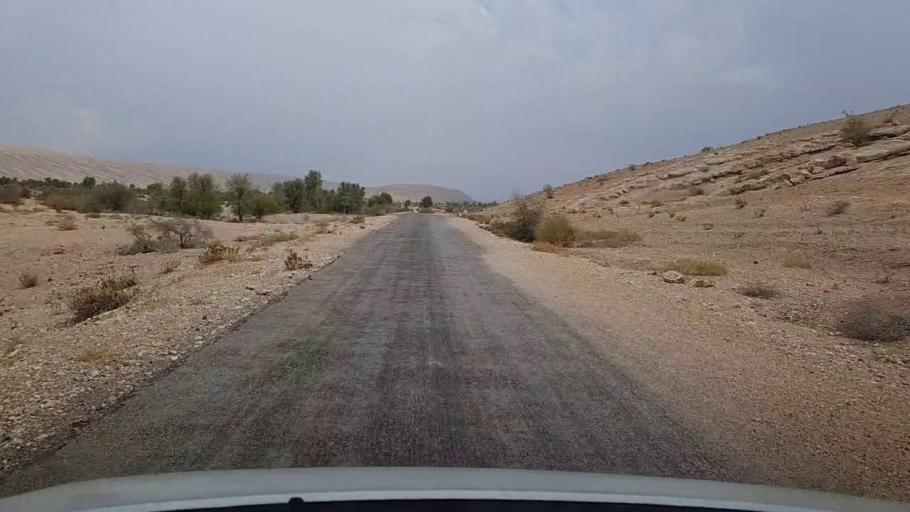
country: PK
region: Sindh
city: Sehwan
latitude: 26.2220
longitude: 67.7136
